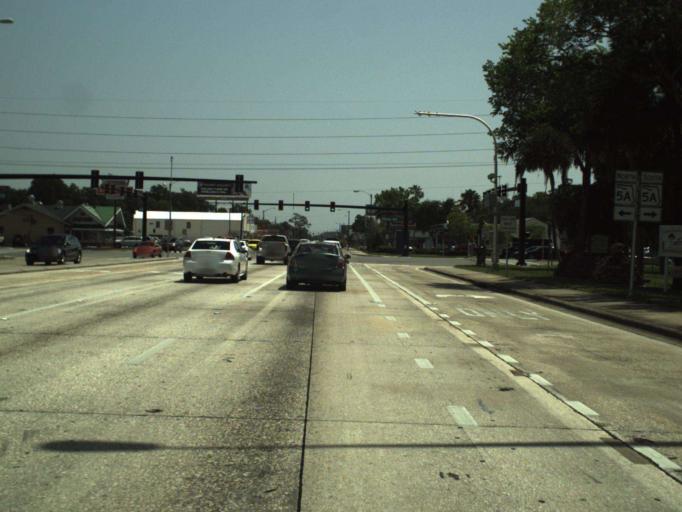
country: US
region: Florida
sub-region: Volusia County
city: Daytona Beach
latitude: 29.2029
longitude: -81.0408
